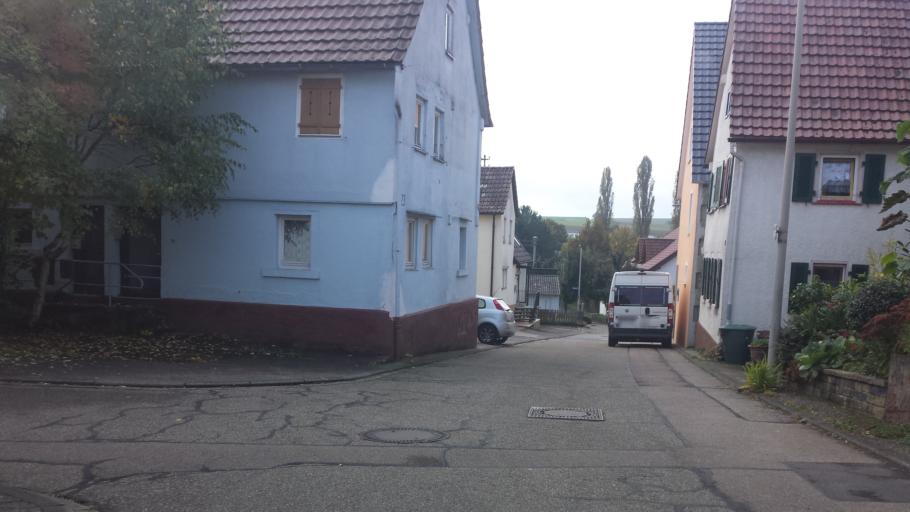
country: DE
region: Baden-Wuerttemberg
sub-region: Regierungsbezirk Stuttgart
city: Bad Rappenau
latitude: 49.2131
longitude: 9.0953
